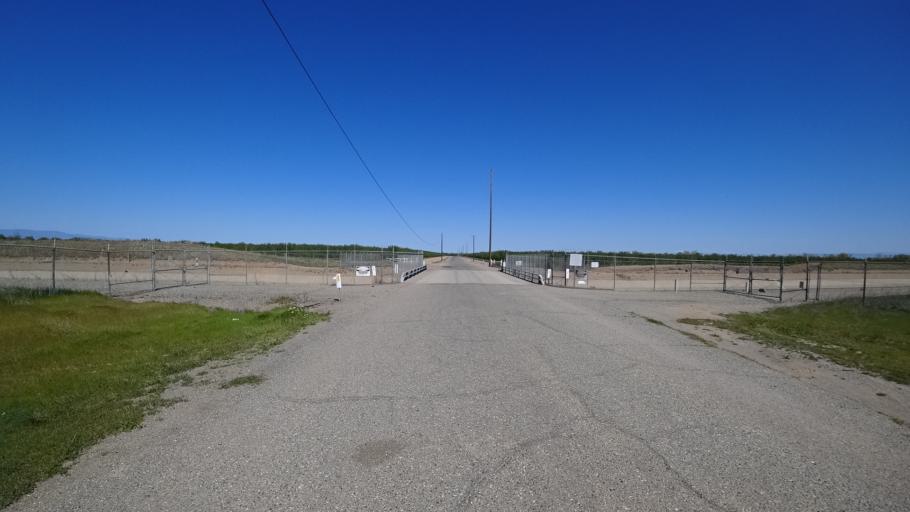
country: US
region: California
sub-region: Glenn County
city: Orland
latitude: 39.6900
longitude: -122.2341
